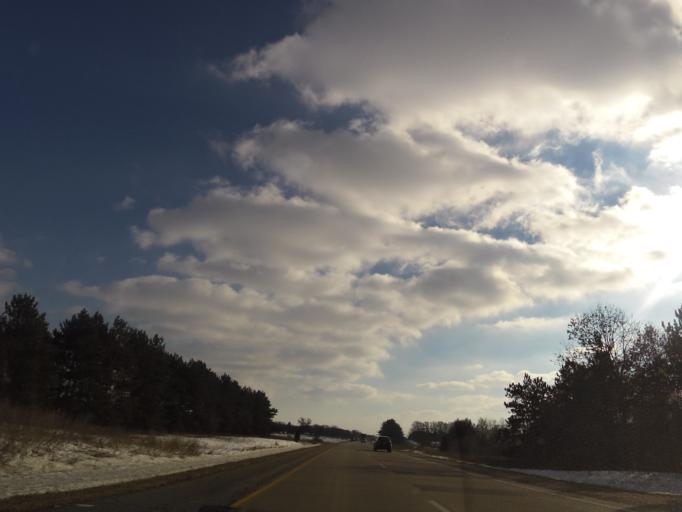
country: US
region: Wisconsin
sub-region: Juneau County
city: Mauston
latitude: 43.8445
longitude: -90.0988
